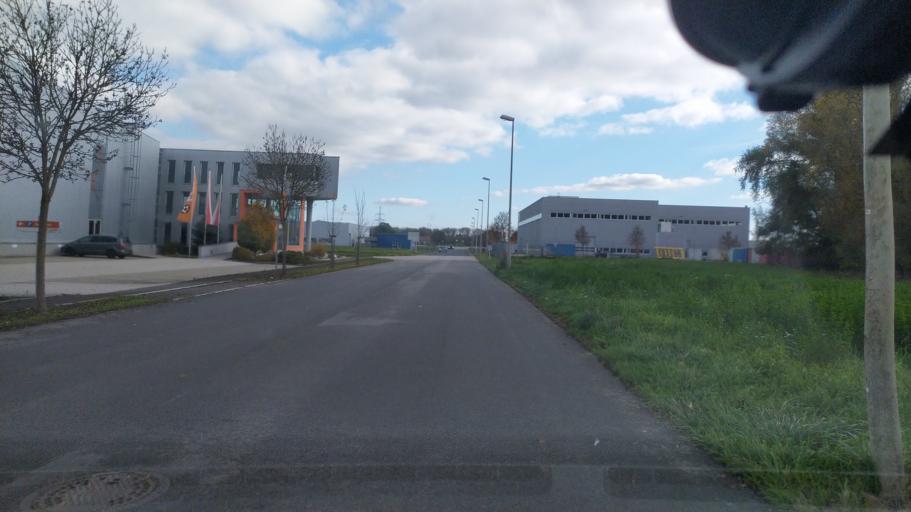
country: AT
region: Upper Austria
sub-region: Politischer Bezirk Urfahr-Umgebung
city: Steyregg
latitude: 48.2502
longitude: 14.3793
